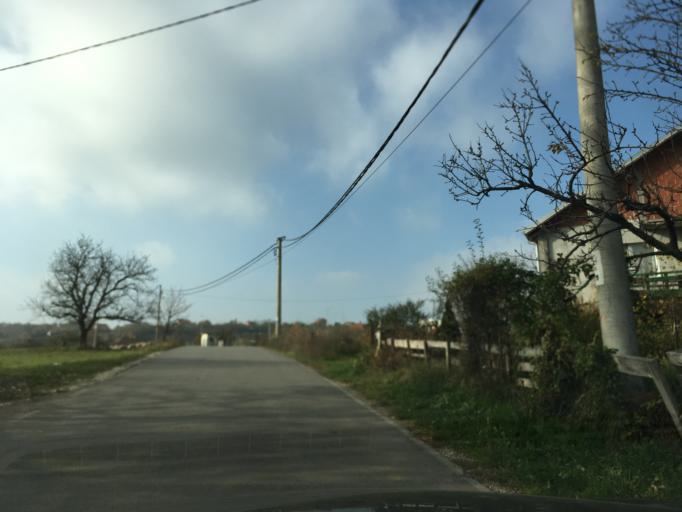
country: RS
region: Central Serbia
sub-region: Belgrade
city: Sopot
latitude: 44.4957
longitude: 20.5816
